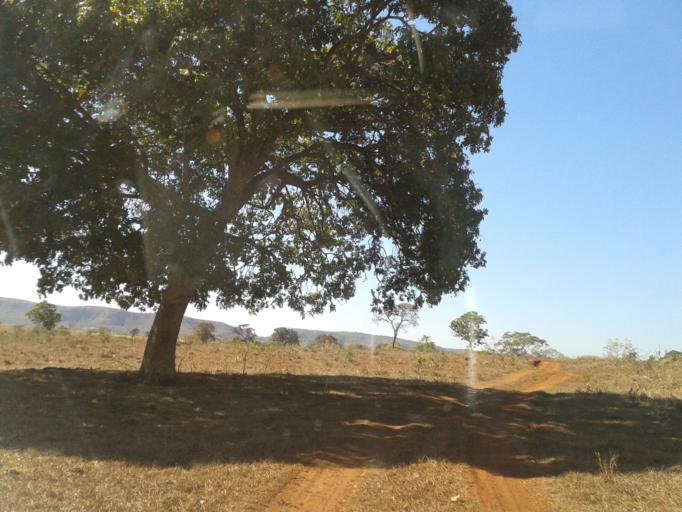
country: BR
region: Minas Gerais
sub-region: Santa Vitoria
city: Santa Vitoria
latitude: -19.0888
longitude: -49.9681
